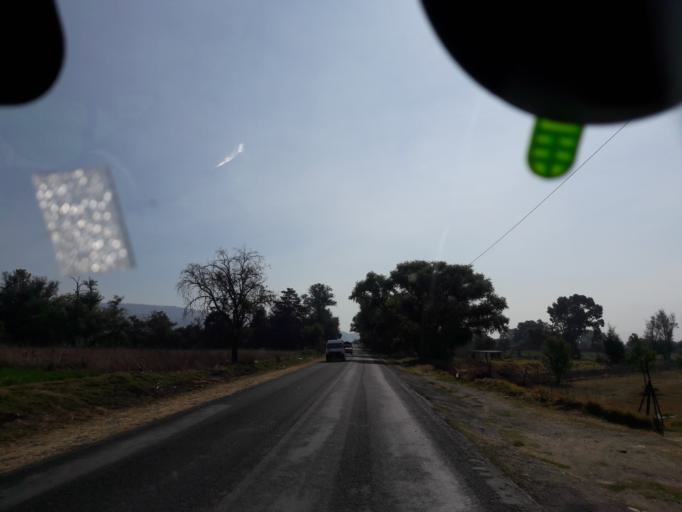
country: MX
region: Tlaxcala
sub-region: Ixtacuixtla de Mariano Matamoros
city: Santa Justina Ecatepec
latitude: 19.3158
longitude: -98.3243
